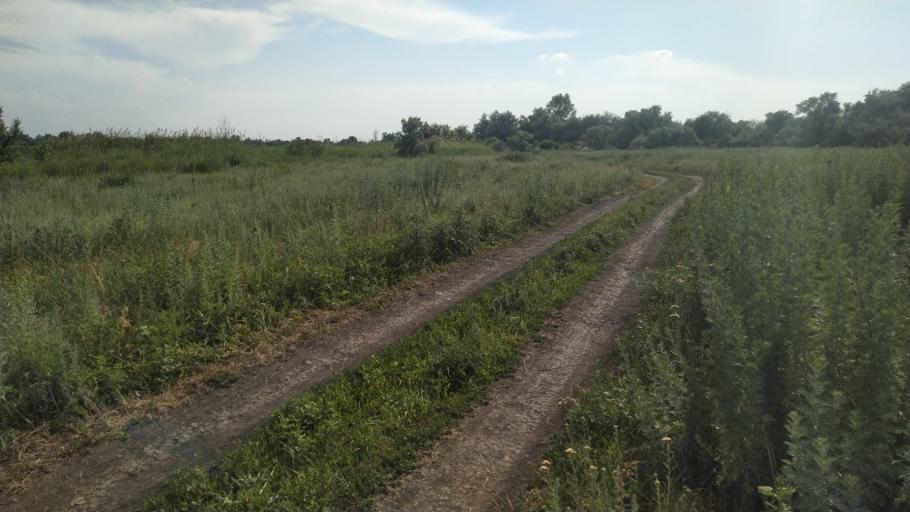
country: RU
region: Rostov
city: Kuleshovka
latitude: 47.1277
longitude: 39.6093
